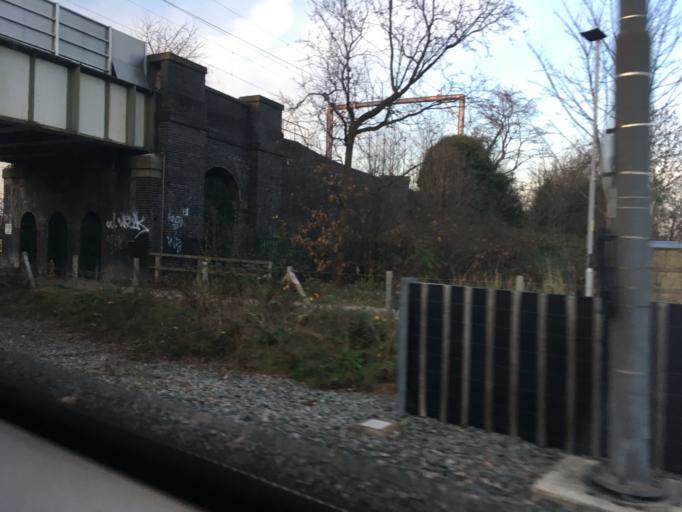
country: GB
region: England
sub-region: Manchester
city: Didsbury
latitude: 53.4129
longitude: -2.2198
